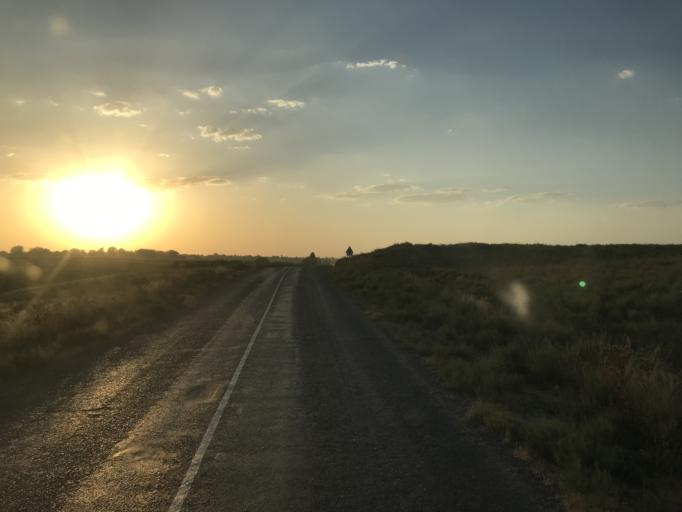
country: UZ
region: Toshkent
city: Yangiyul
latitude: 41.3508
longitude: 68.8669
